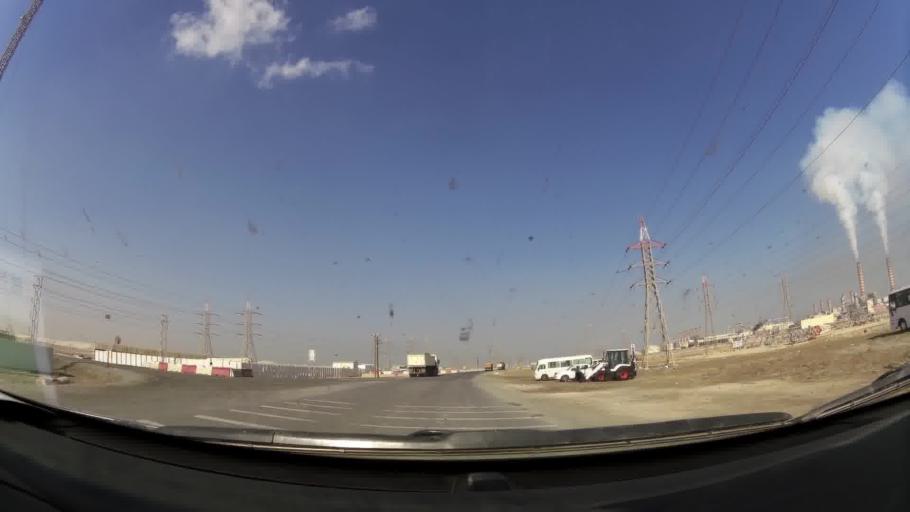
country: SA
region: Eastern Province
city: Al Khafji
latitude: 28.6983
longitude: 48.3584
